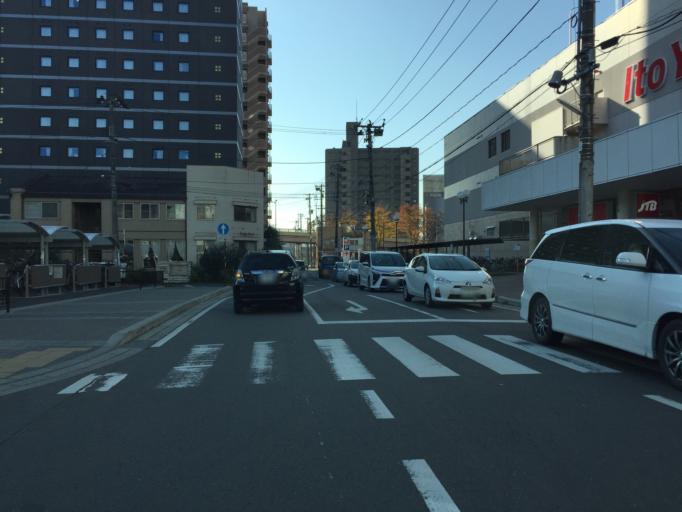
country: JP
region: Fukushima
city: Fukushima-shi
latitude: 37.7542
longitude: 140.4576
